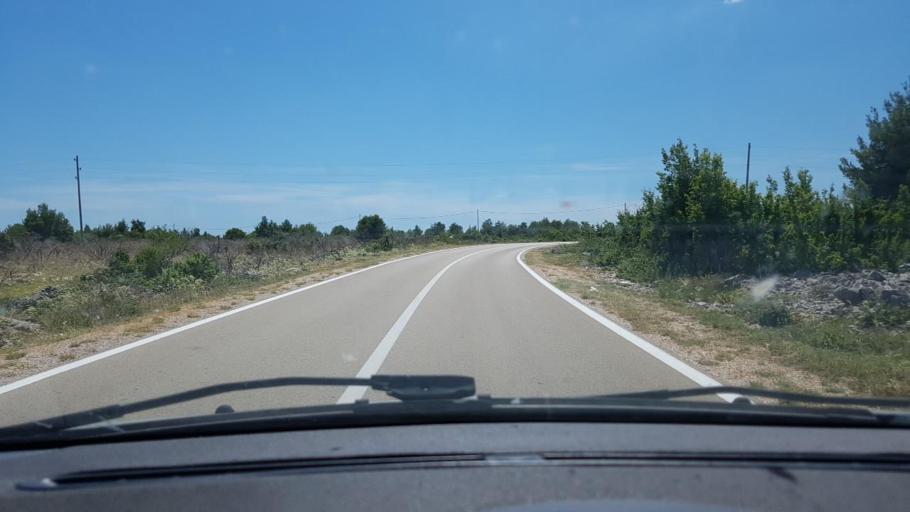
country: HR
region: Sibensko-Kniniska
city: Kistanje
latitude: 43.9130
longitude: 15.9326
